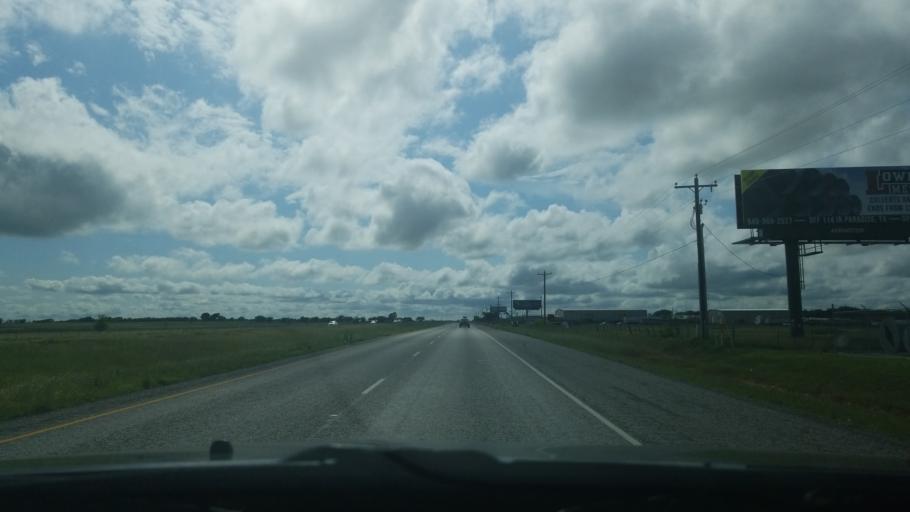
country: US
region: Texas
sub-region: Denton County
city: Ponder
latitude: 33.2388
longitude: -97.3229
